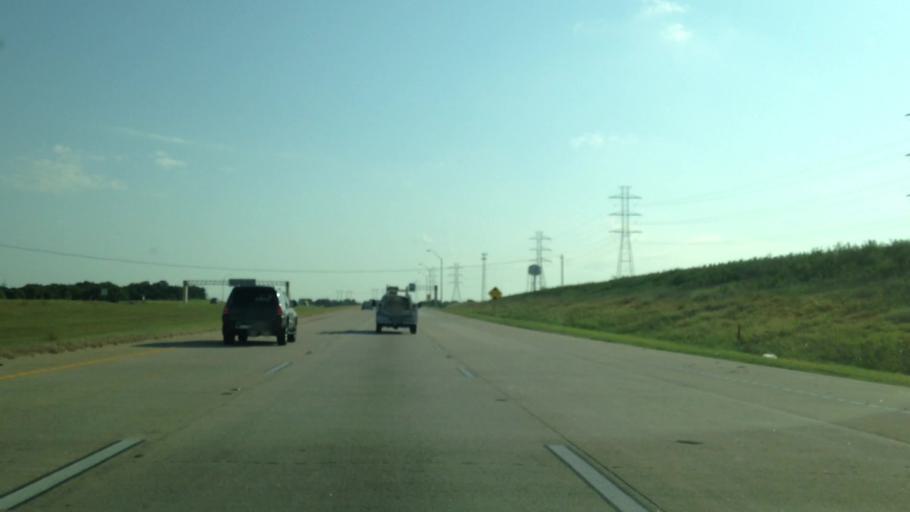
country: US
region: Texas
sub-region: Travis County
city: Hornsby Bend
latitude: 30.2743
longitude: -97.5859
